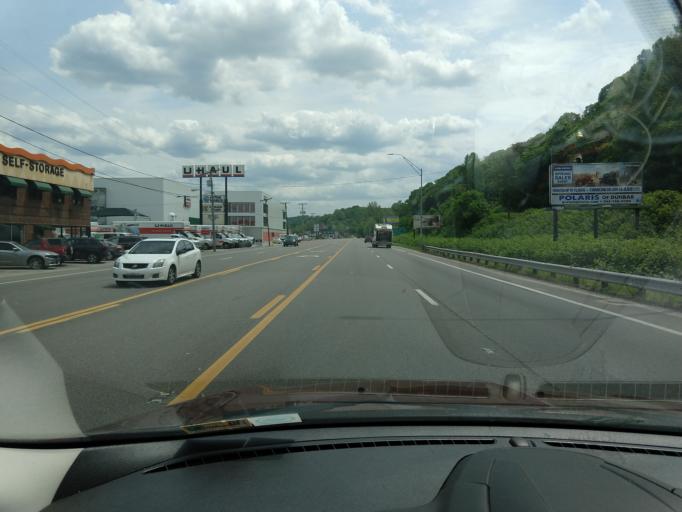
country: US
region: West Virginia
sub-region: Kanawha County
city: Dunbar
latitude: 38.3622
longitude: -81.7604
